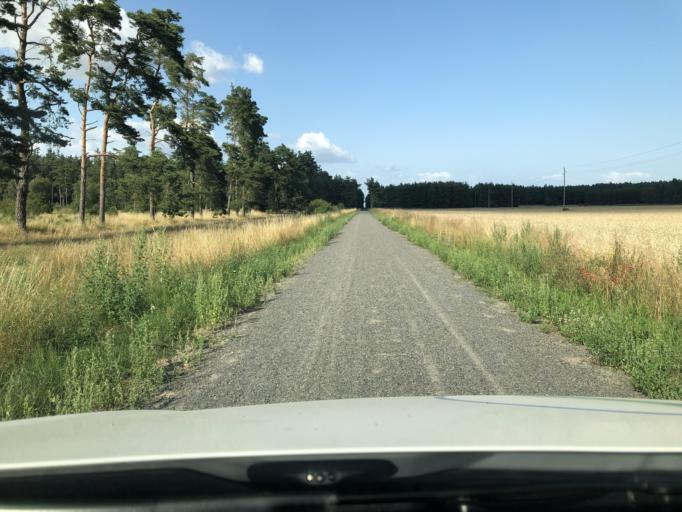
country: SE
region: Skane
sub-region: Kristianstads Kommun
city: Norra Asum
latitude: 55.9203
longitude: 14.1224
